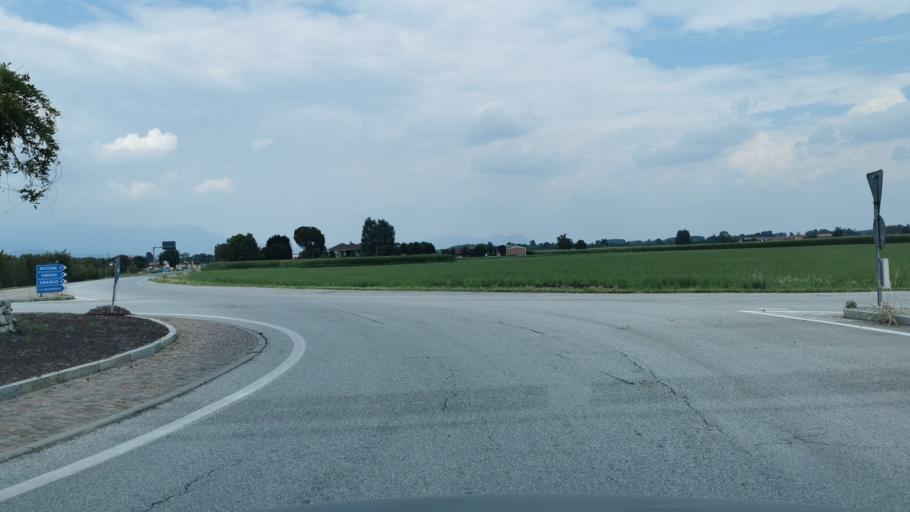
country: IT
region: Piedmont
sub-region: Provincia di Torino
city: Garzigliana
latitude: 44.8166
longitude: 7.3714
